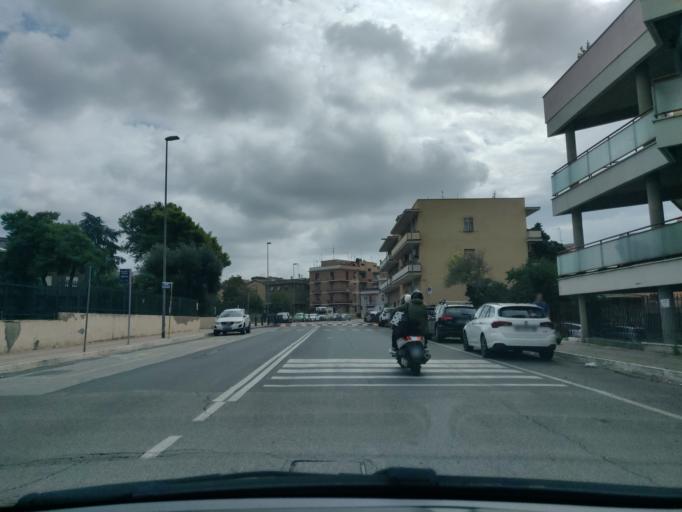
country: IT
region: Latium
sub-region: Citta metropolitana di Roma Capitale
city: Civitavecchia
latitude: 42.0947
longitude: 11.8043
